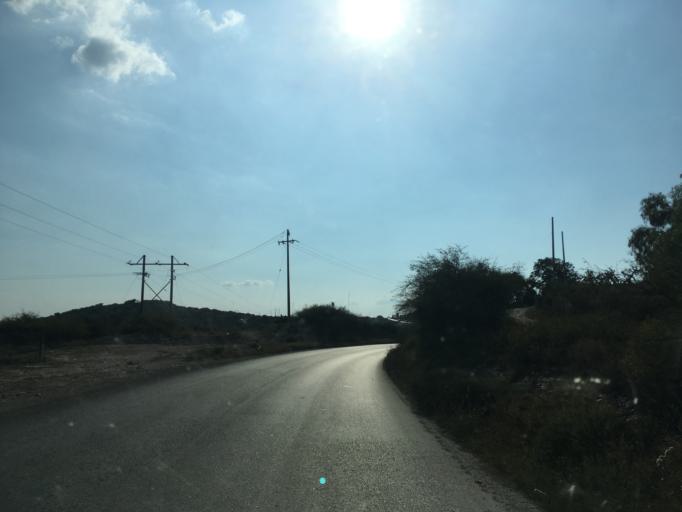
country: MX
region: Hidalgo
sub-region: Ixmiquilpan
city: El Nith
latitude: 20.5744
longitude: -99.1407
